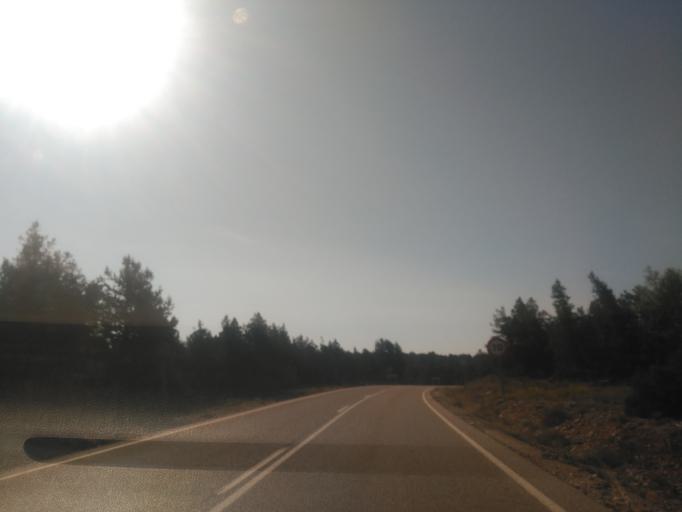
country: ES
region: Castille and Leon
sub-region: Provincia de Soria
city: Ucero
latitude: 41.7336
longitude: -3.0423
